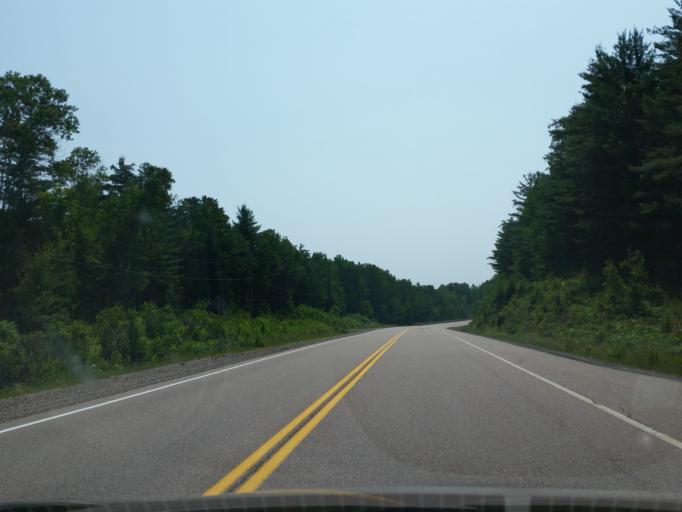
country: CA
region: Ontario
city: Deep River
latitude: 46.2107
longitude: -77.8899
